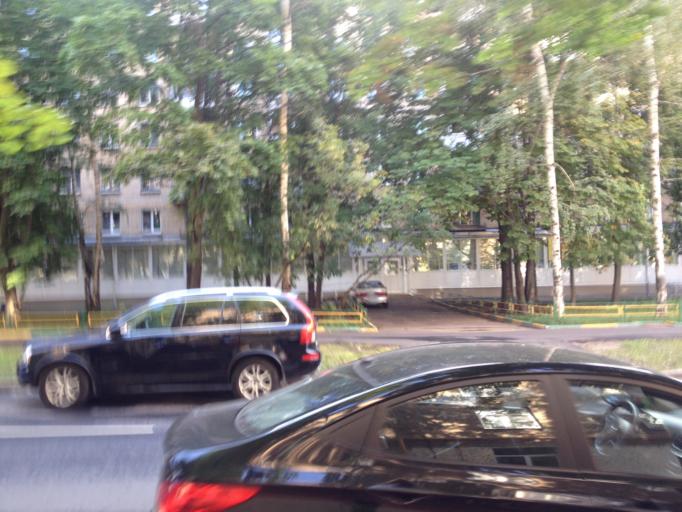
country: RU
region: Moskovskaya
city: Izmaylovo
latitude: 55.7907
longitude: 37.7882
